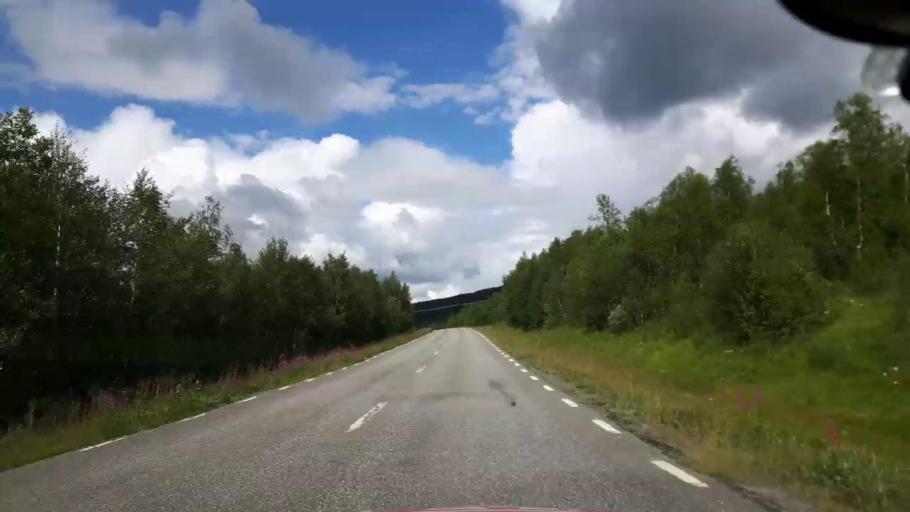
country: NO
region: Nordland
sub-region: Hattfjelldal
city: Hattfjelldal
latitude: 65.0589
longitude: 14.7169
